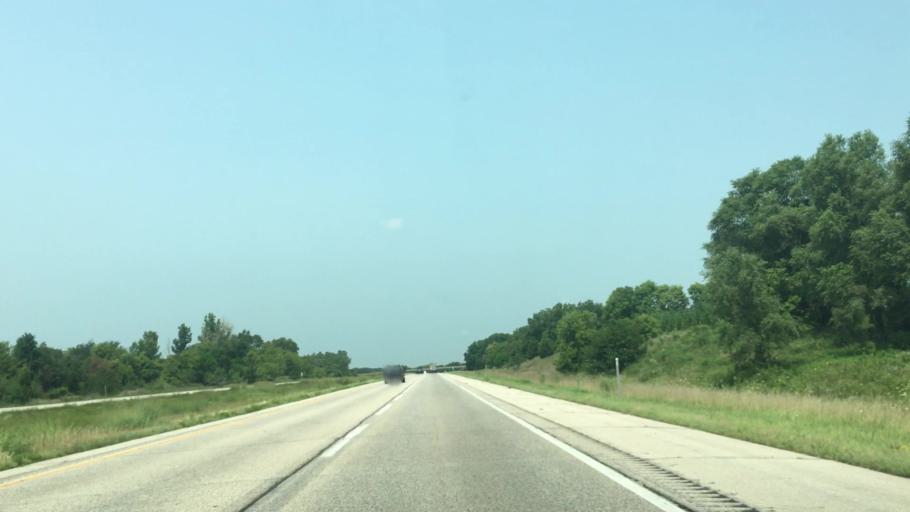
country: US
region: Iowa
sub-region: Linn County
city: Robins
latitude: 42.1193
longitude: -91.7132
